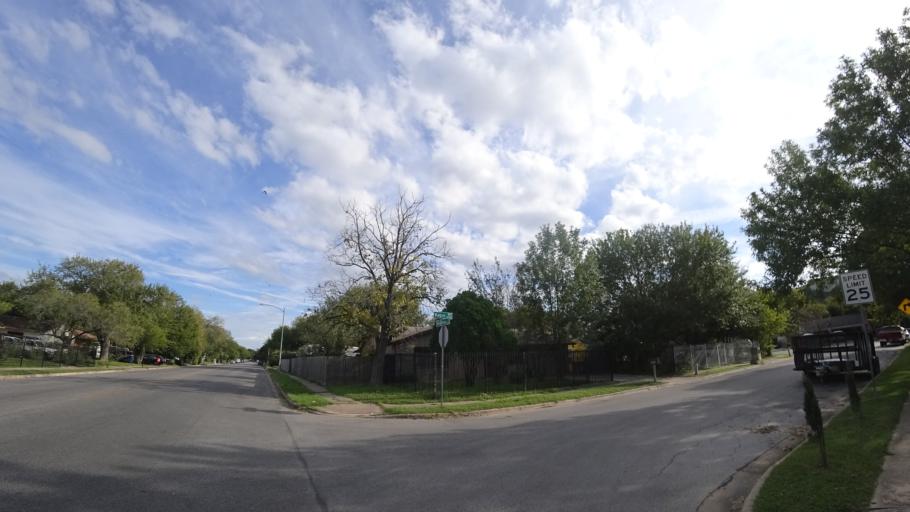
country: US
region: Texas
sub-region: Travis County
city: Onion Creek
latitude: 30.1892
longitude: -97.7551
